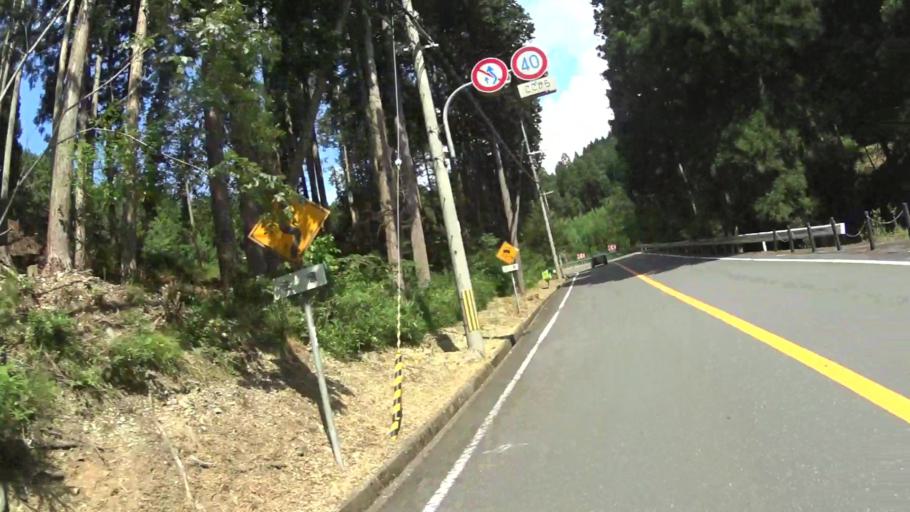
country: JP
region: Kyoto
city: Kameoka
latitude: 35.2761
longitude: 135.5646
